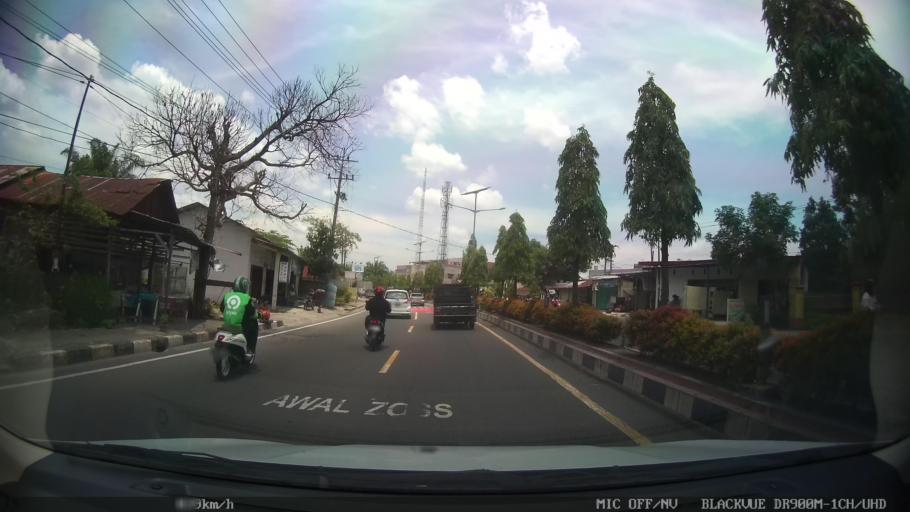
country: ID
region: North Sumatra
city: Binjai
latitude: 3.6054
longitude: 98.5302
